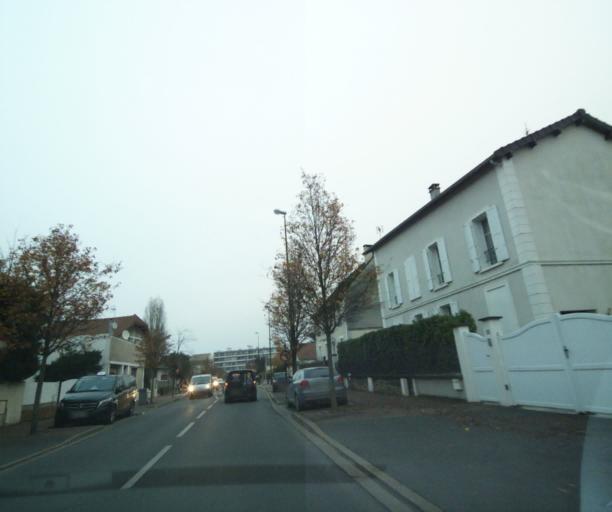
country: FR
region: Ile-de-France
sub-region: Departement de Seine-Saint-Denis
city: Livry-Gargan
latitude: 48.9168
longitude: 2.5367
